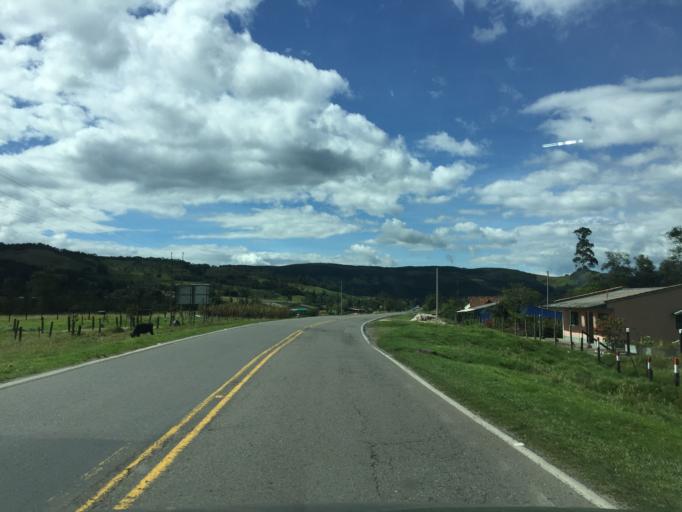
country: CO
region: Boyaca
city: Arcabuco
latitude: 5.7749
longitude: -73.4584
